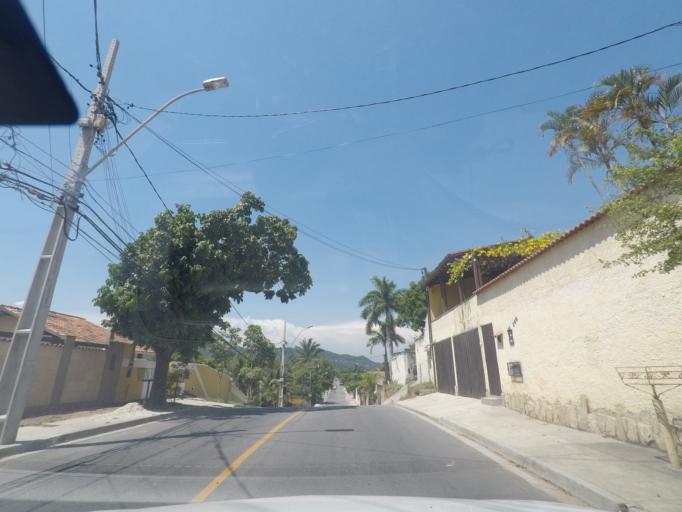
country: BR
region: Rio de Janeiro
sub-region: Niteroi
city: Niteroi
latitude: -22.9452
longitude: -43.0285
